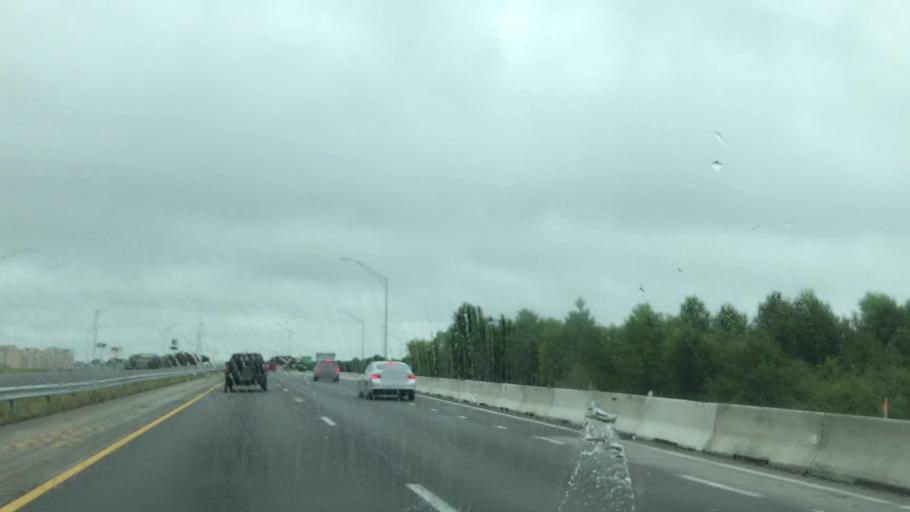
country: US
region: North Carolina
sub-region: Halifax County
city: Weldon
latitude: 36.4267
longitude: -77.6308
